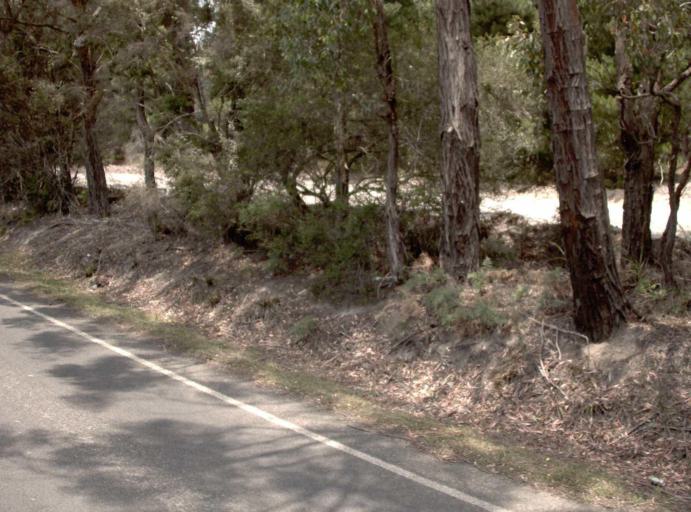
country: AU
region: Victoria
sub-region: Latrobe
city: Traralgon
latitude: -38.2622
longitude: 146.6817
